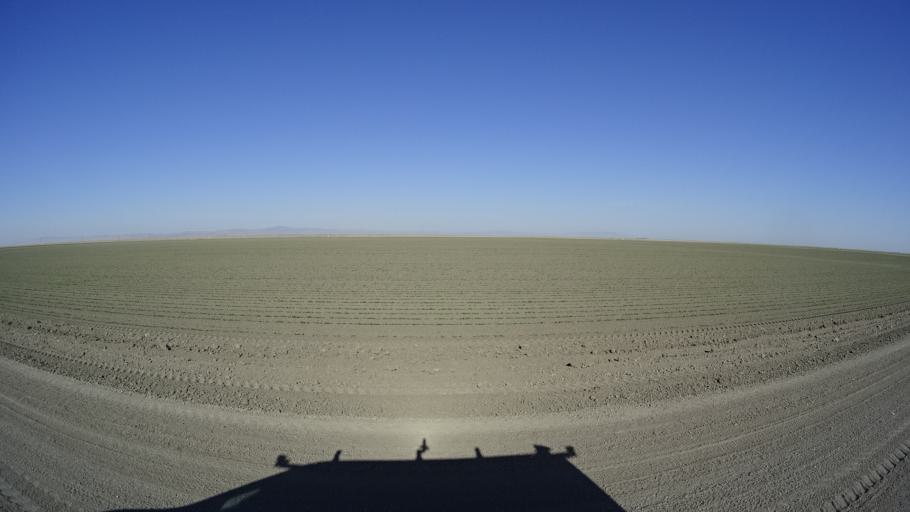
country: US
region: California
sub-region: Kings County
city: Stratford
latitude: 36.0836
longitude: -119.7979
